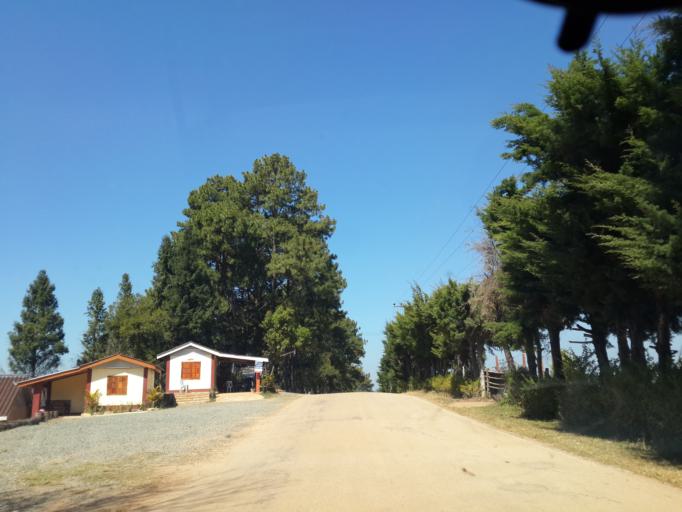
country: TH
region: Chiang Mai
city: Fang
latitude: 19.9321
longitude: 99.0428
